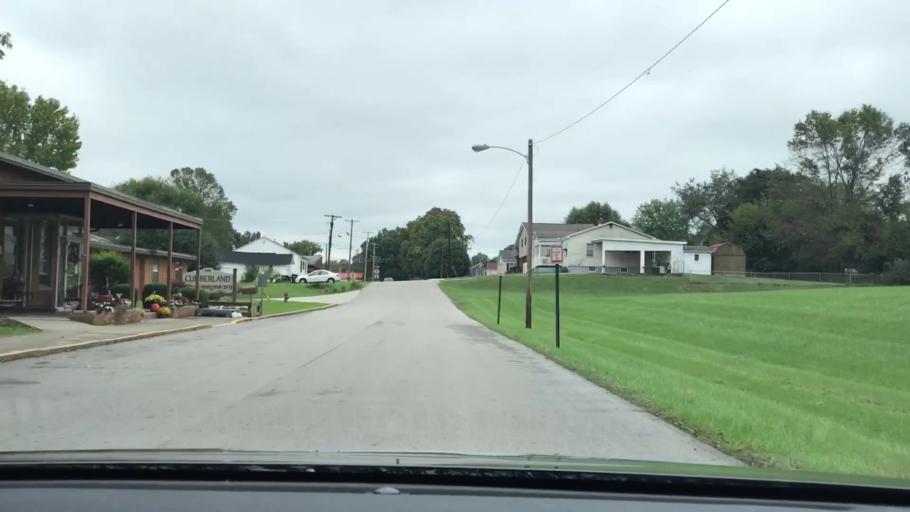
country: US
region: Kentucky
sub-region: Pulaski County
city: Somerset
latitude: 37.0843
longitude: -84.5971
